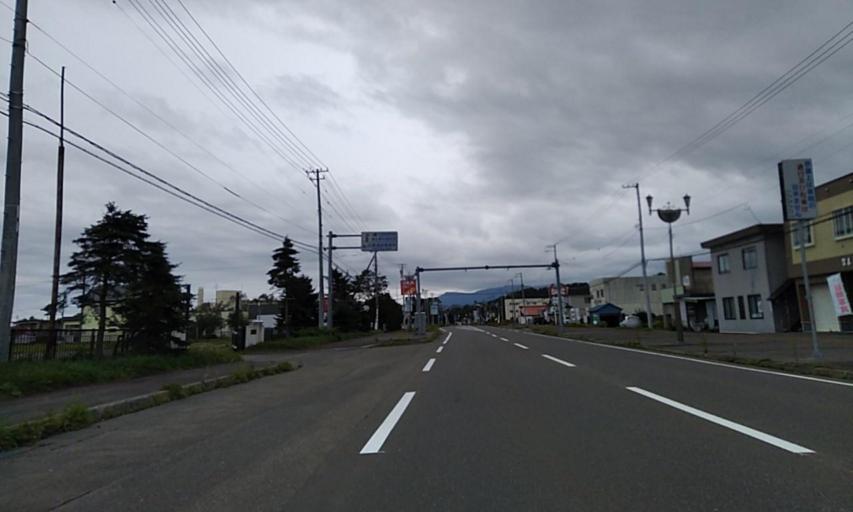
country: JP
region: Hokkaido
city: Obihiro
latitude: 42.2996
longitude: 143.3150
